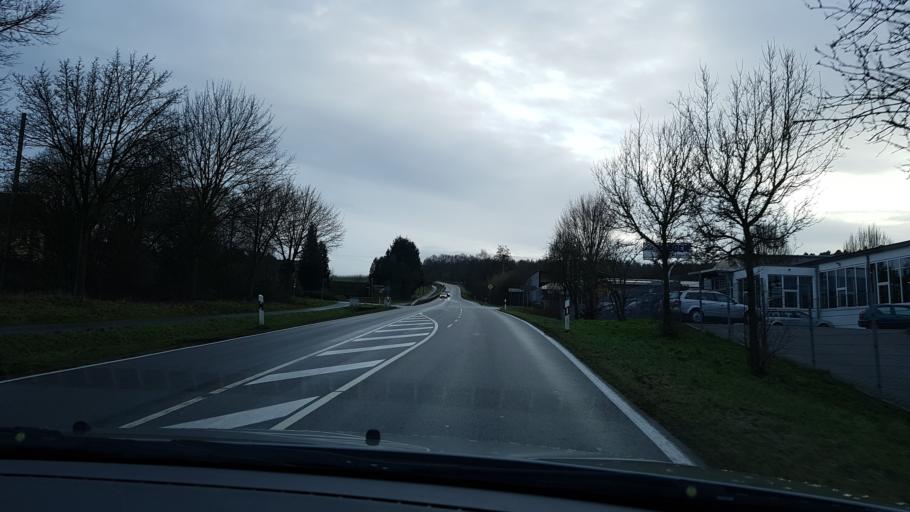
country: DE
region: Rheinland-Pfalz
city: Niederelbert
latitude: 50.4016
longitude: 7.8121
